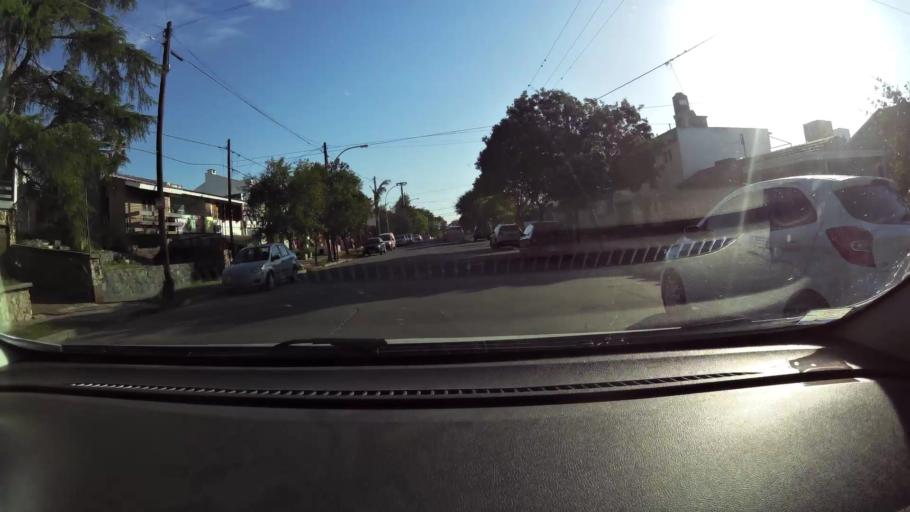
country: AR
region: Cordoba
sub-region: Departamento de Capital
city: Cordoba
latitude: -31.3777
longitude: -64.2429
